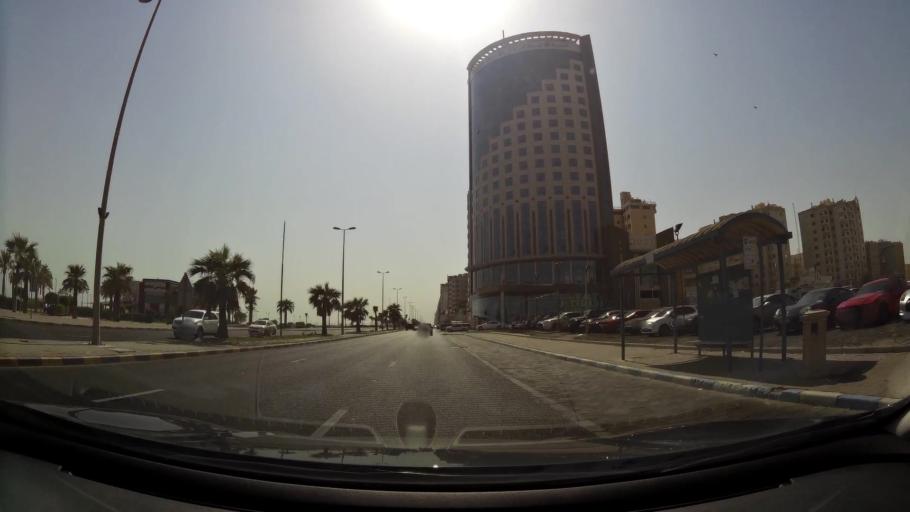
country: KW
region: Muhafazat Hawalli
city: As Salimiyah
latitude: 29.3411
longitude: 48.0963
